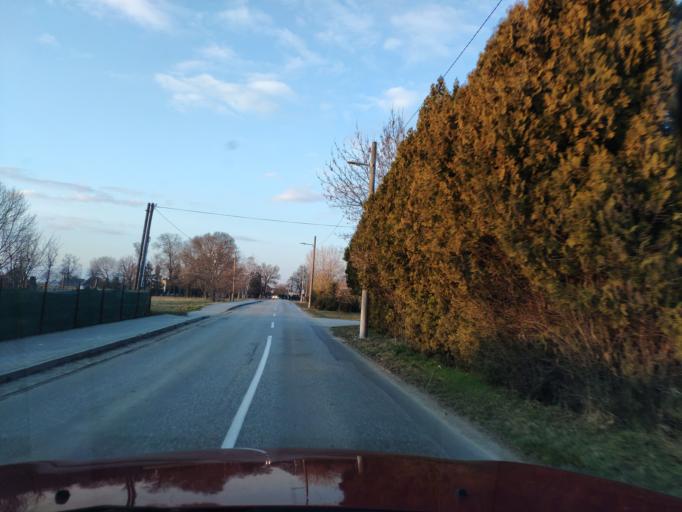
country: SK
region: Nitriansky
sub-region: Okres Nitra
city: Nitra
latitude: 48.2107
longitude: 18.0709
